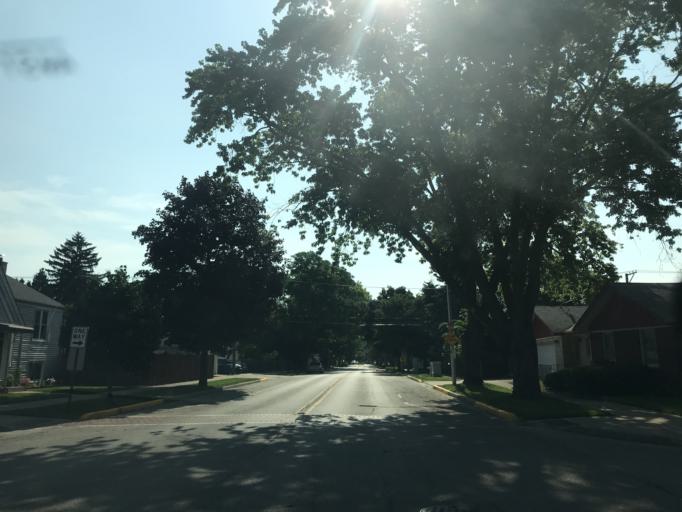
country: US
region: Illinois
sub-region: Cook County
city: Forest Park
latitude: 41.8686
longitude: -87.8095
